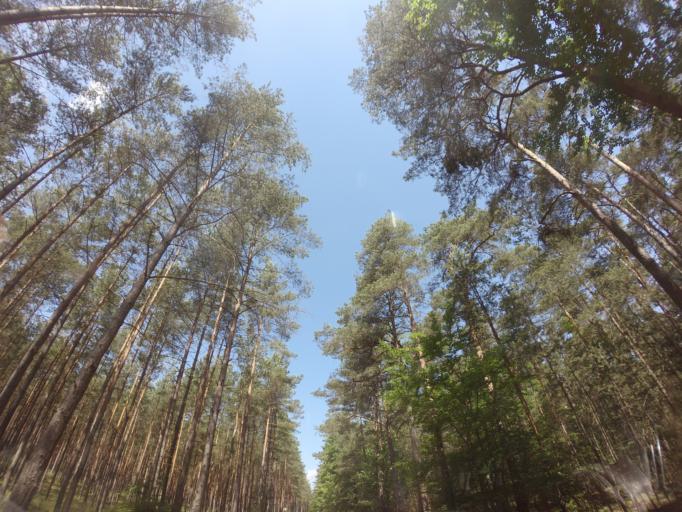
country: PL
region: West Pomeranian Voivodeship
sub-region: Powiat choszczenski
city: Drawno
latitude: 53.1538
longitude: 15.8057
